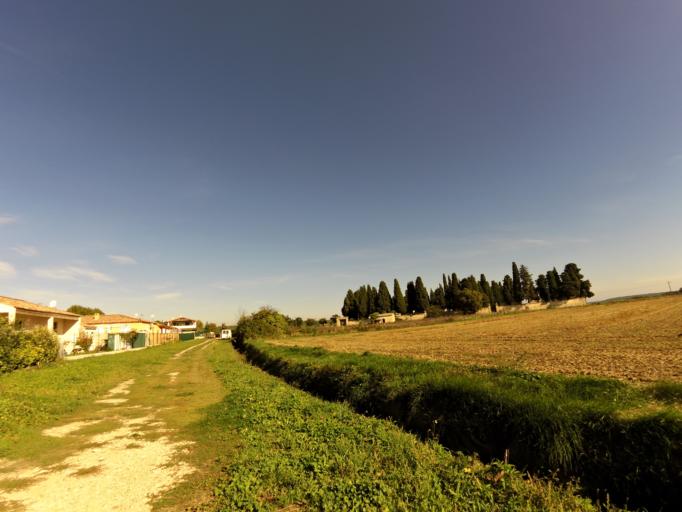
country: FR
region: Languedoc-Roussillon
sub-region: Departement du Gard
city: Aigues-Vives
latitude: 43.7439
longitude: 4.1829
